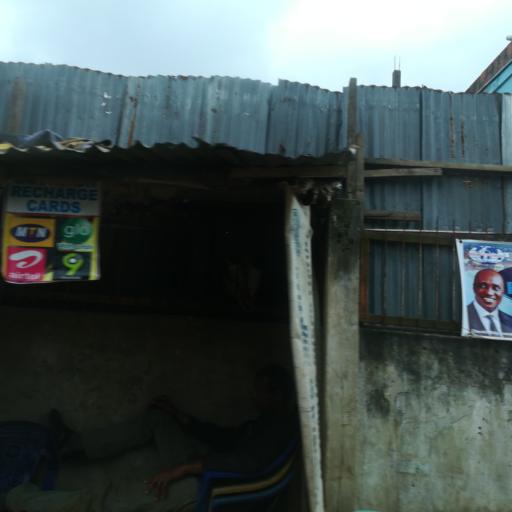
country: NG
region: Lagos
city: Agege
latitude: 6.6043
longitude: 3.2945
